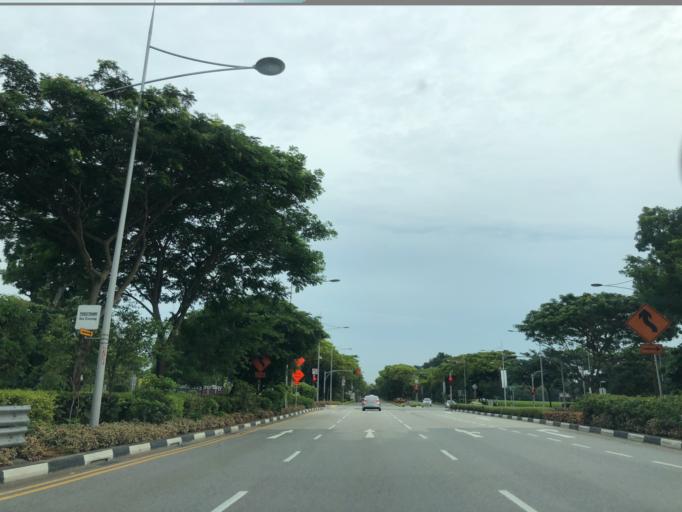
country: SG
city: Singapore
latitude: 1.2750
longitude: 103.8614
